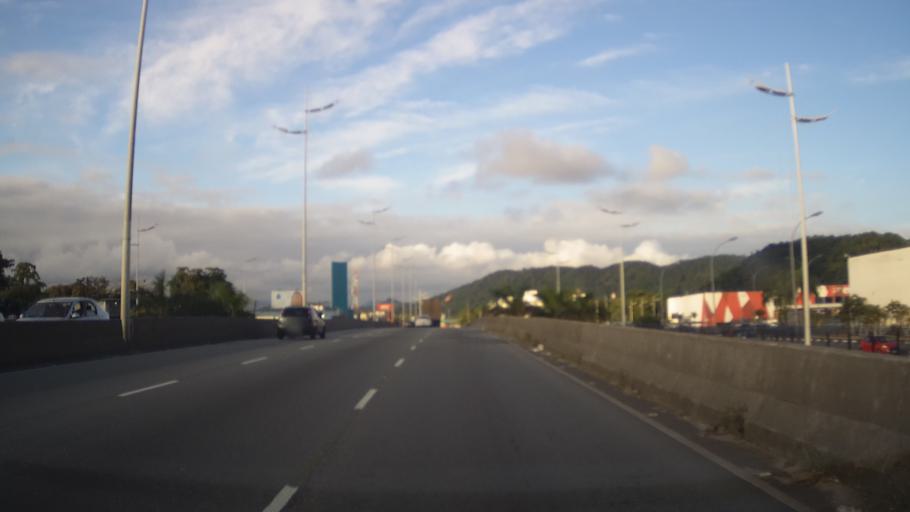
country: BR
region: Sao Paulo
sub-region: Praia Grande
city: Praia Grande
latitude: -23.9969
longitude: -46.4097
